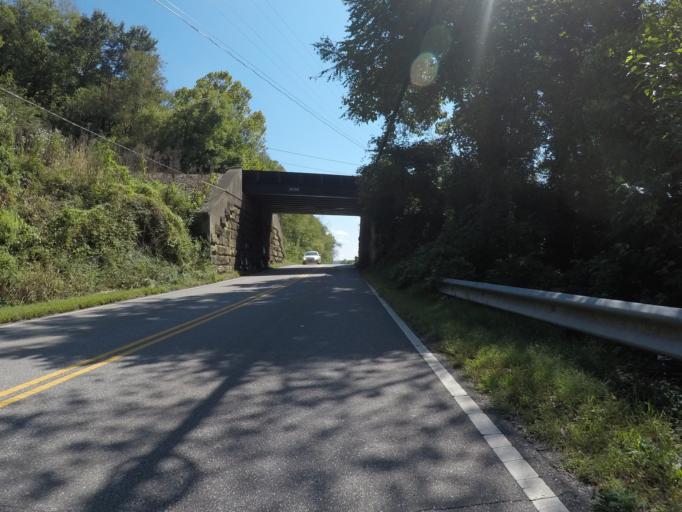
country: US
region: West Virginia
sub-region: Wayne County
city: Kenova
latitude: 38.4084
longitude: -82.5722
